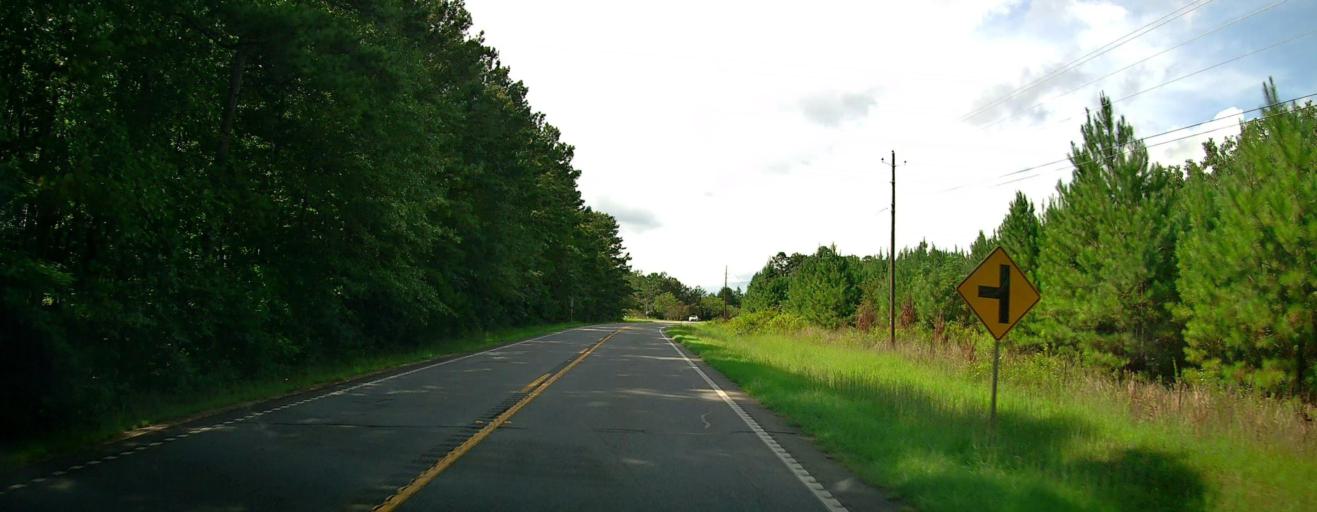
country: US
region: Georgia
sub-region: Talbot County
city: Sardis
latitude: 32.8226
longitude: -84.6127
